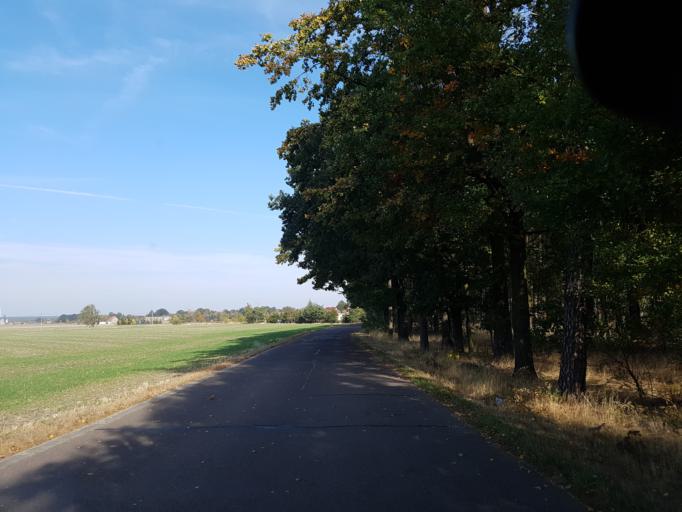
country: DE
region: Brandenburg
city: Schonborn
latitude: 51.6627
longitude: 13.5033
